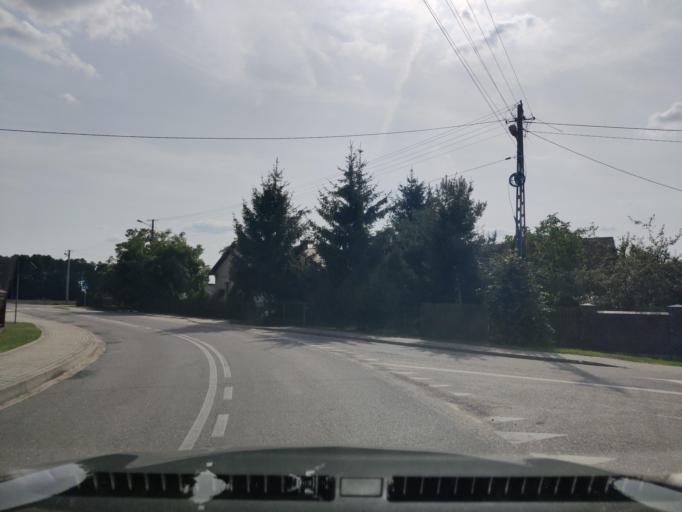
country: PL
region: Masovian Voivodeship
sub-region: Powiat wyszkowski
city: Rzasnik
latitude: 52.7628
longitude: 21.3540
